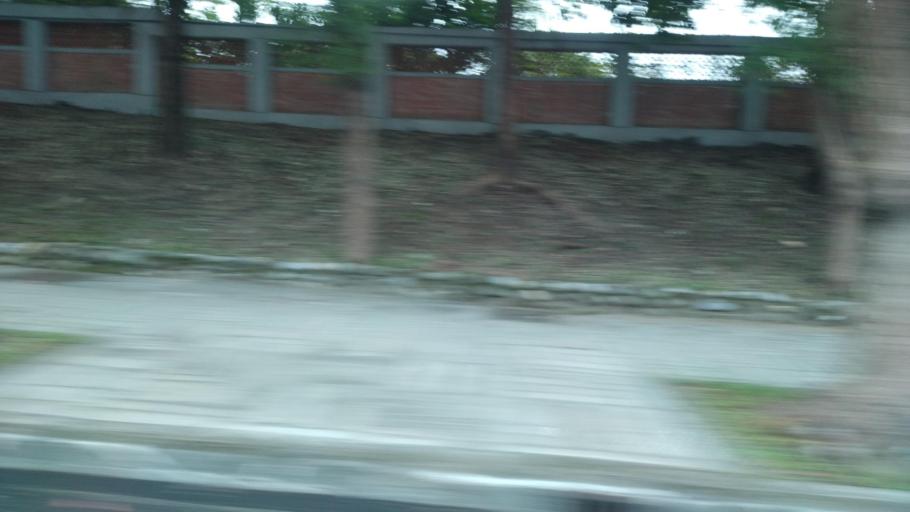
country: TW
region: Taiwan
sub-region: Hualien
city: Hualian
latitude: 24.0017
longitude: 121.6198
